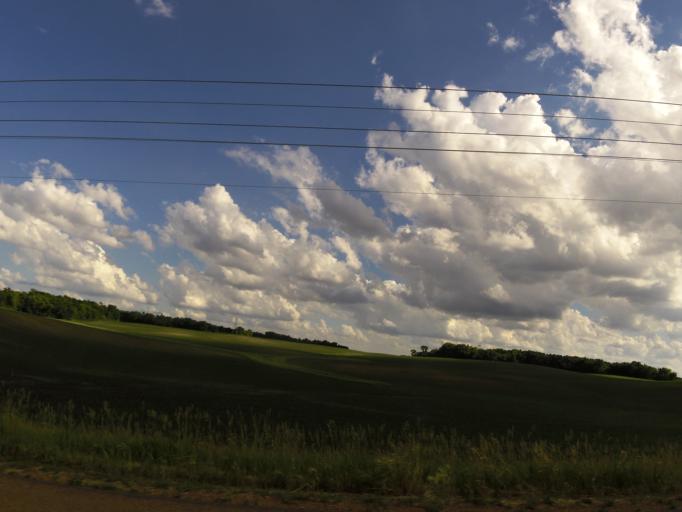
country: US
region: Minnesota
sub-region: Carver County
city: Waconia
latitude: 44.8188
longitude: -93.7265
